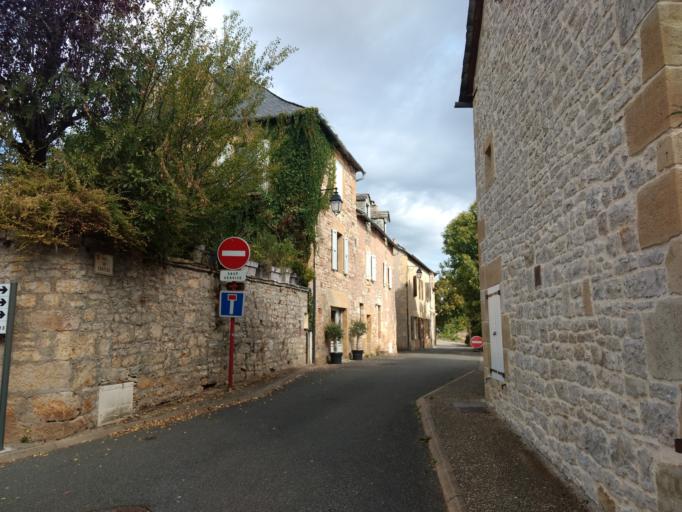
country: FR
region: Midi-Pyrenees
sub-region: Departement de l'Aveyron
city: Bozouls
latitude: 44.4682
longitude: 2.7157
